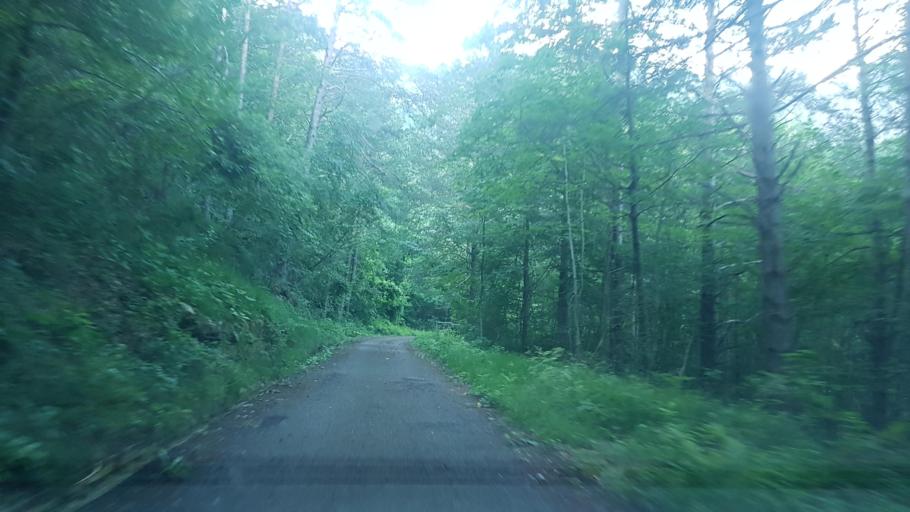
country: IT
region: Friuli Venezia Giulia
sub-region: Provincia di Udine
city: Paularo
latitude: 46.4706
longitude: 13.1034
